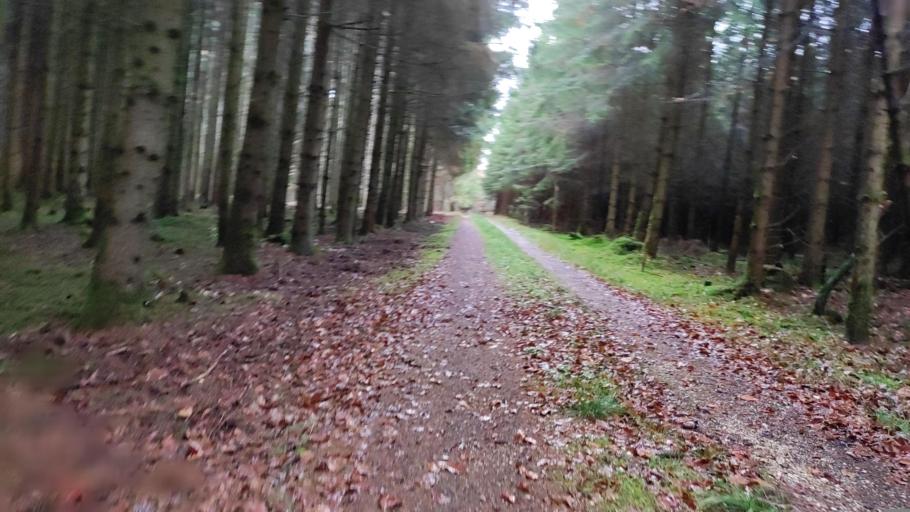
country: DE
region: Bavaria
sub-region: Swabia
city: Burtenbach
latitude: 48.3580
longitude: 10.5028
